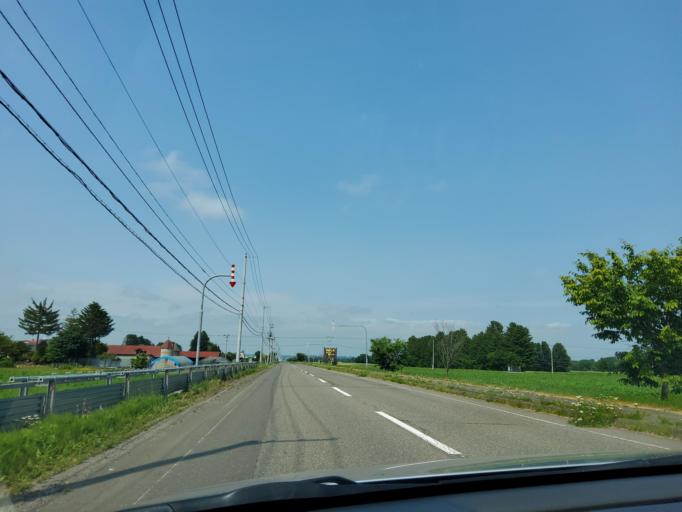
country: JP
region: Hokkaido
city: Obihiro
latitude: 42.8756
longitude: 143.0279
